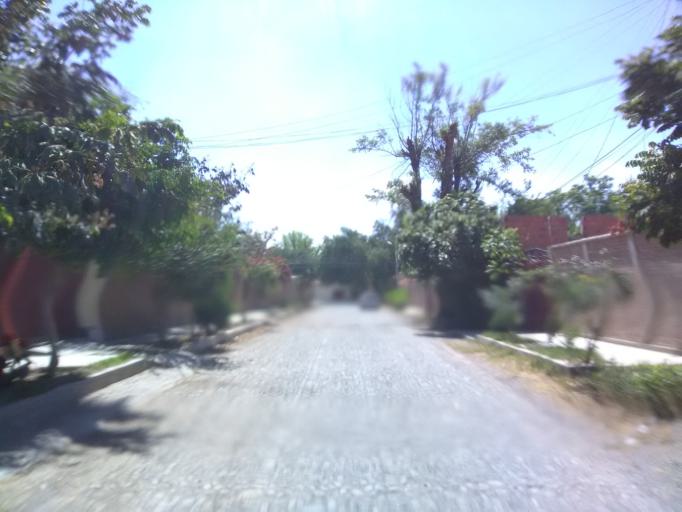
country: BO
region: Cochabamba
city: Cochabamba
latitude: -17.3498
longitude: -66.1999
